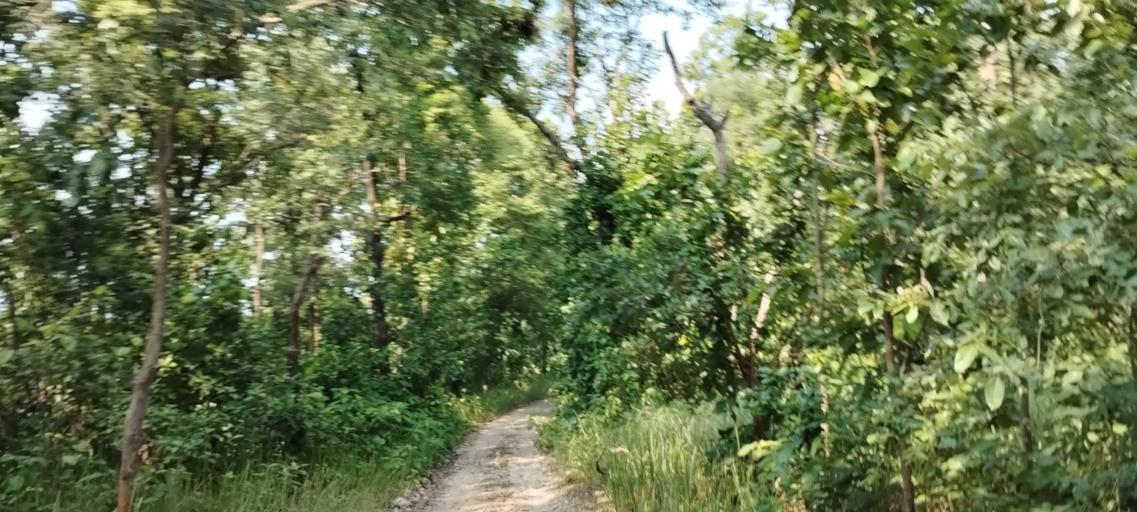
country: NP
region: Far Western
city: Tikapur
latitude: 28.5554
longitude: 81.2634
